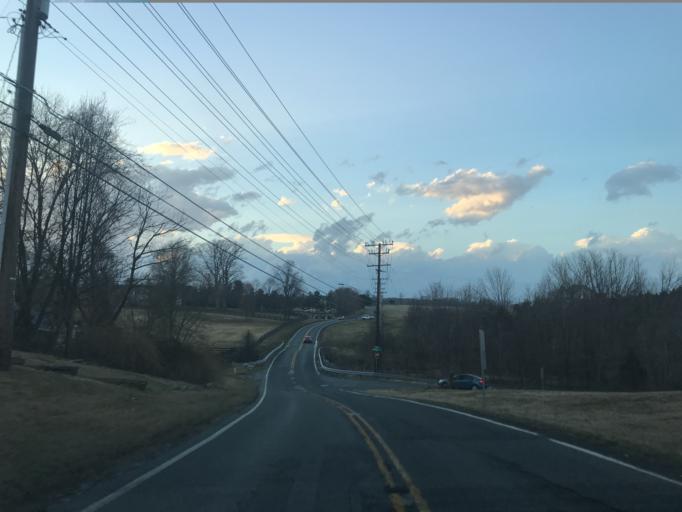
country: US
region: Maryland
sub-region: Harford County
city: Bel Air South
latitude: 39.5351
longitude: -76.2818
